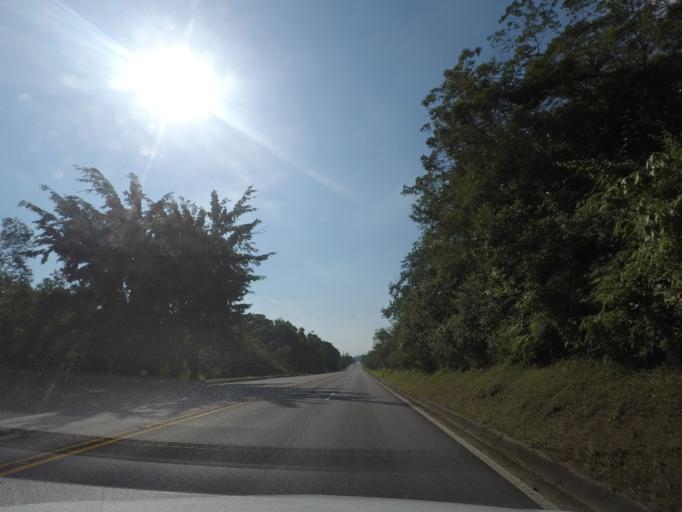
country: BR
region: Parana
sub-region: Paranagua
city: Paranagua
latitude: -25.5950
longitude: -48.6107
